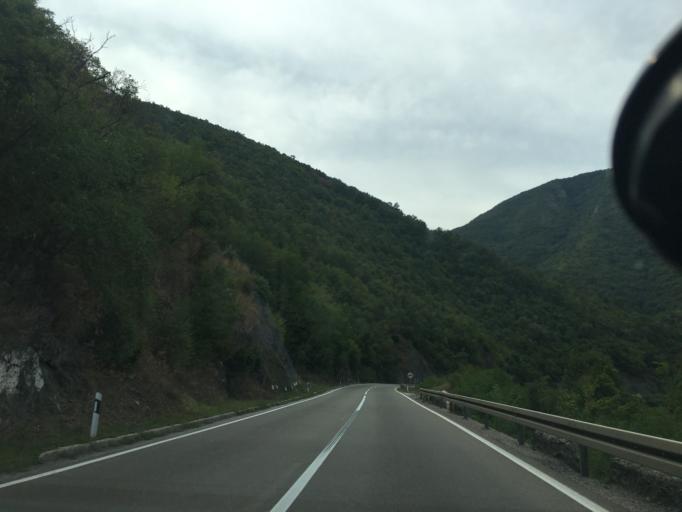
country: RS
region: Central Serbia
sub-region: Moravicki Okrug
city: Lucani
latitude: 43.9139
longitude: 20.2225
